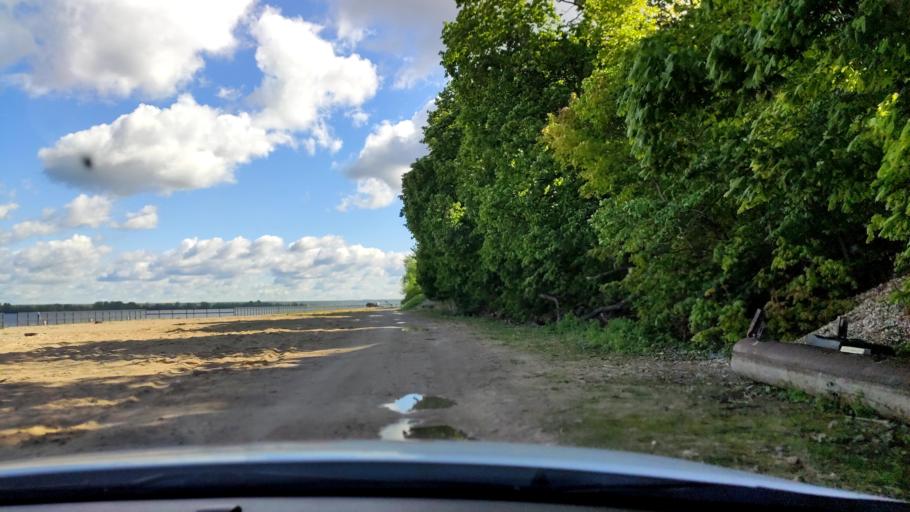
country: RU
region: Tatarstan
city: Sviyazhsk
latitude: 55.7817
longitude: 48.6996
